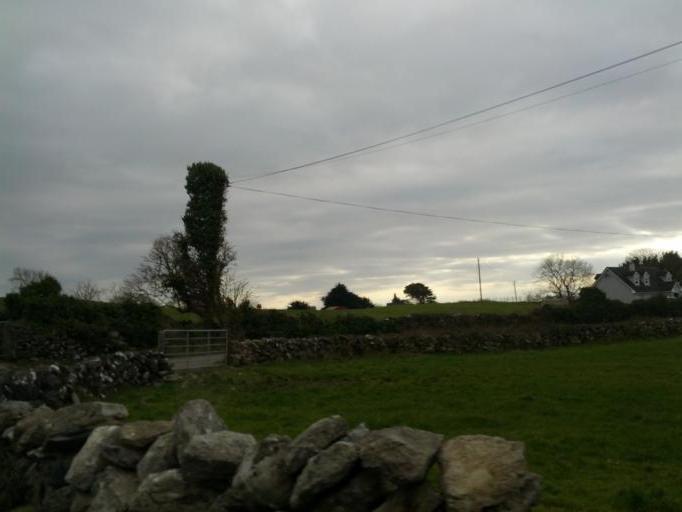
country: IE
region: Connaught
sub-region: County Galway
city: Oranmore
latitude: 53.2031
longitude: -8.9112
